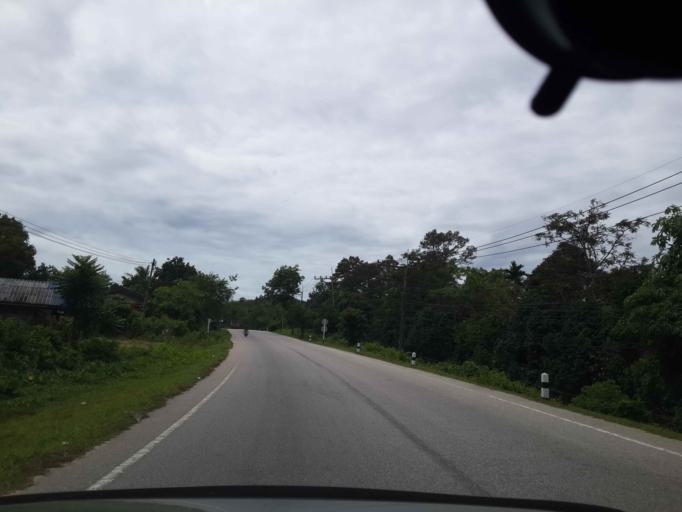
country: TH
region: Narathiwat
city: Rueso
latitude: 6.3680
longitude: 101.5985
